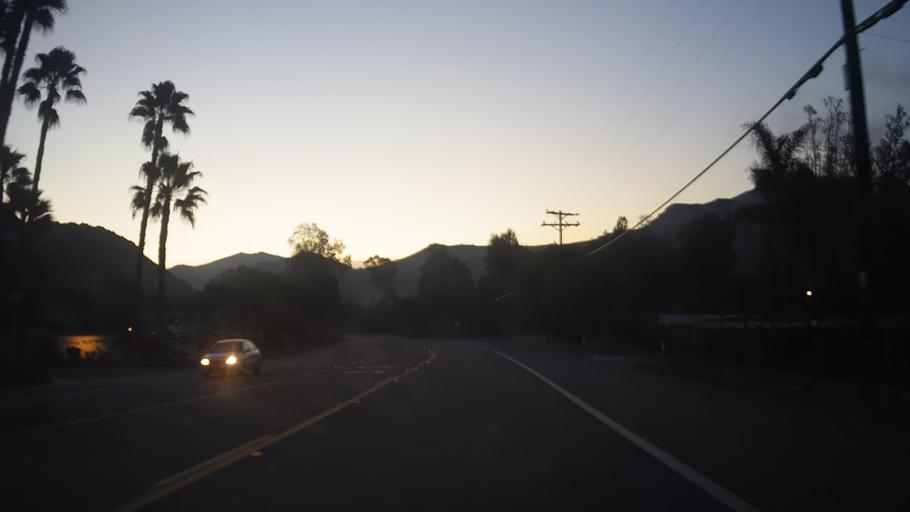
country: US
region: California
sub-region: San Diego County
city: Crest
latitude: 32.7821
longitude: -116.8758
